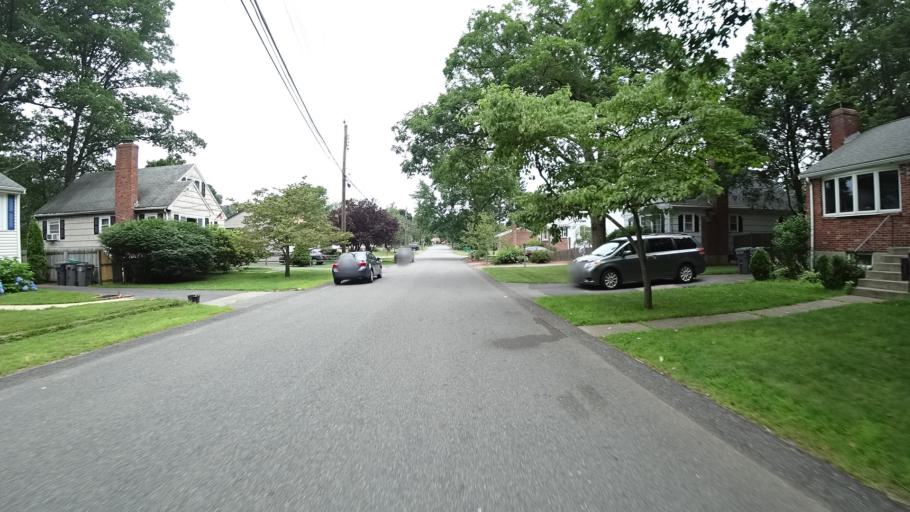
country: US
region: Massachusetts
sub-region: Norfolk County
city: Dedham
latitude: 42.2227
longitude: -71.1626
